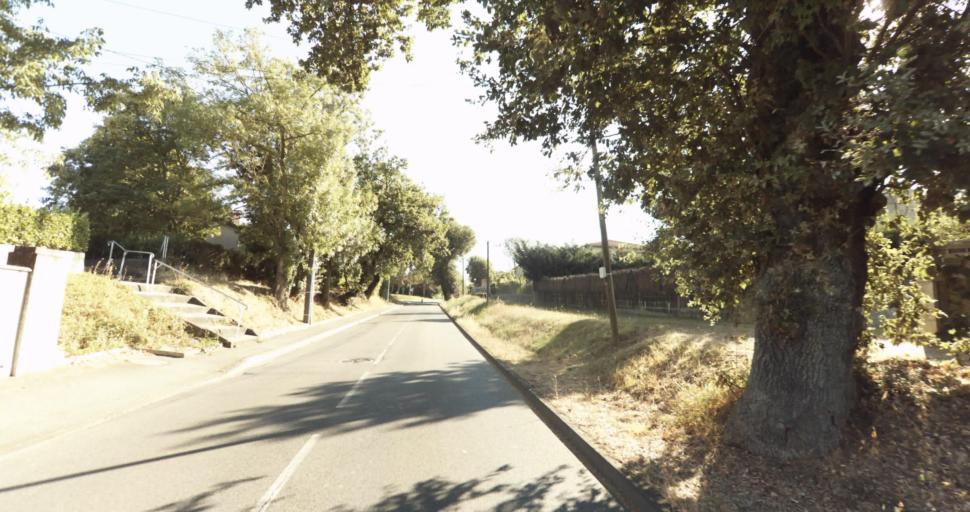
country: FR
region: Midi-Pyrenees
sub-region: Departement de la Haute-Garonne
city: L'Union
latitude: 43.6628
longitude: 1.4863
